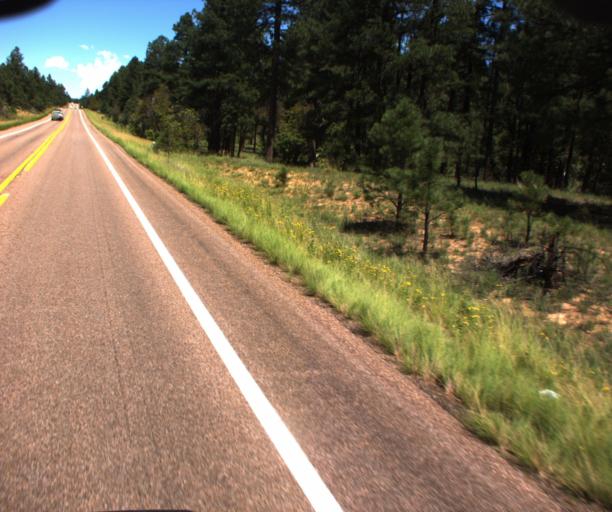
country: US
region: Arizona
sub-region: Navajo County
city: Lake of the Woods
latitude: 34.1529
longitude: -110.1024
